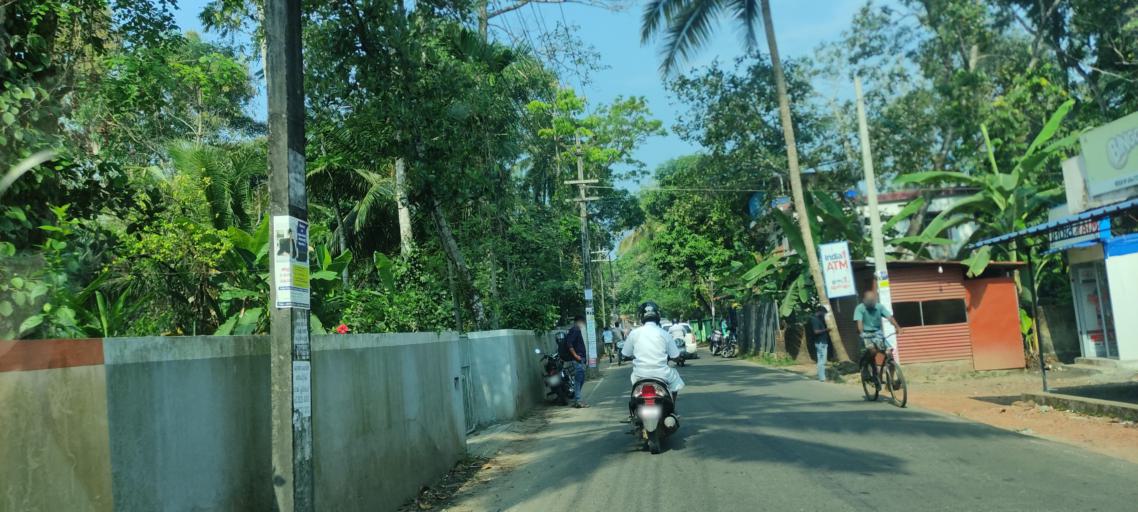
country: IN
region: Kerala
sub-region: Alappuzha
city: Kutiatodu
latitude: 9.7692
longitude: 76.3101
